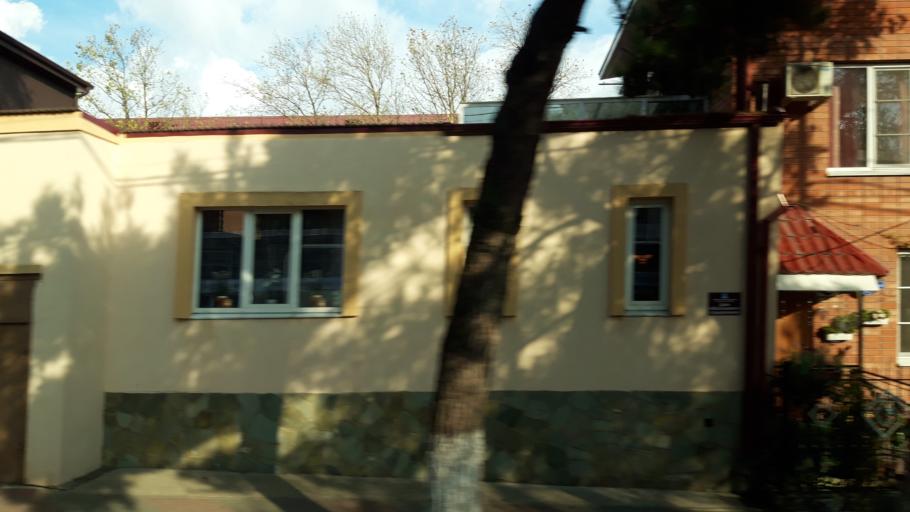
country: RU
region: Krasnodarskiy
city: Gelendzhik
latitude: 44.5537
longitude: 38.0719
